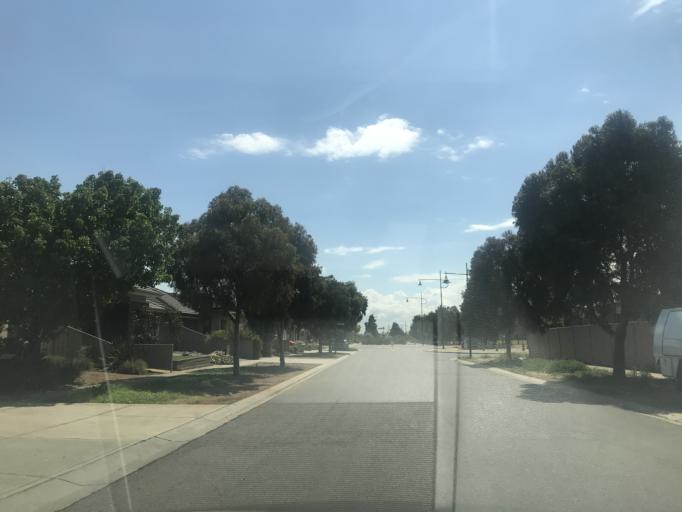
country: AU
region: Victoria
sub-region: Wyndham
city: Hoppers Crossing
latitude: -37.8876
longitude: 144.7204
